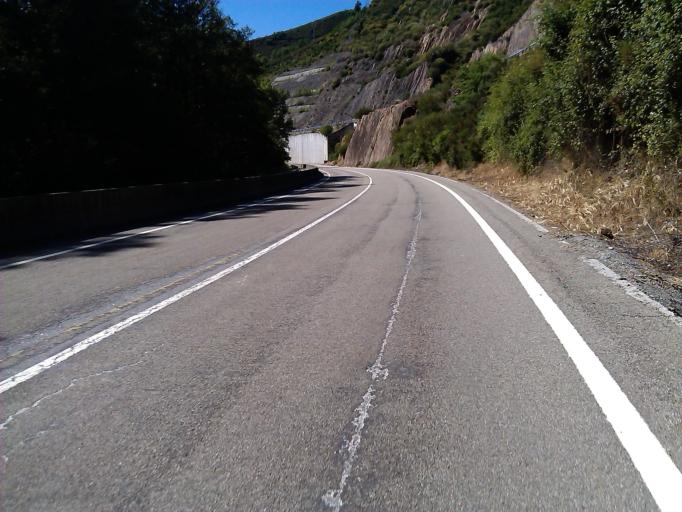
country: ES
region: Castille and Leon
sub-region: Provincia de Leon
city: Trabadelo
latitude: 42.6369
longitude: -6.8546
